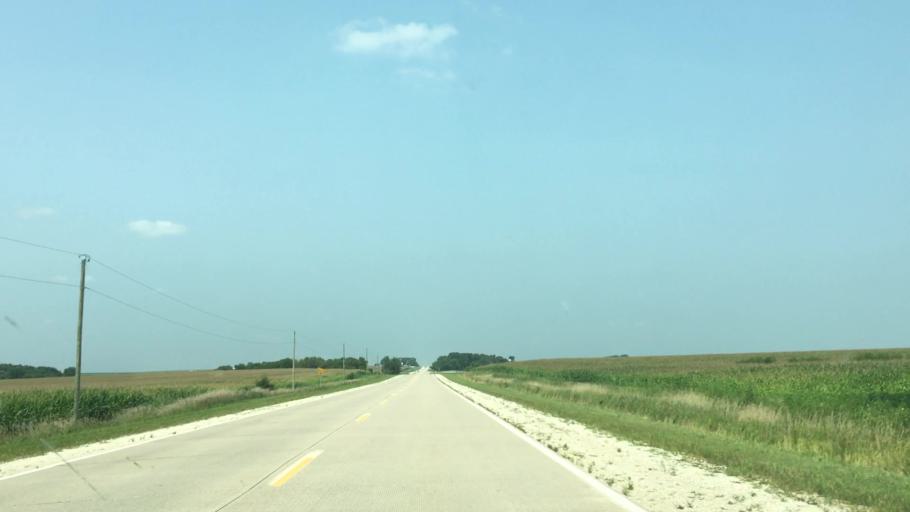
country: US
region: Iowa
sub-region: Fayette County
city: Fayette
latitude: 42.7519
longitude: -91.8042
